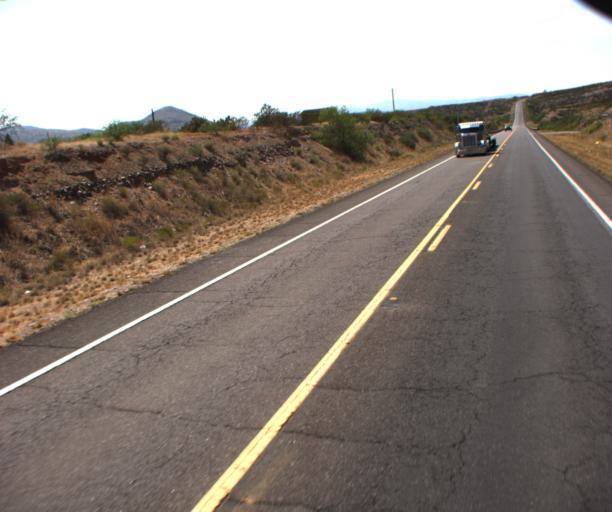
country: US
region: Arizona
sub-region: Greenlee County
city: Clifton
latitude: 32.9384
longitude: -109.2179
